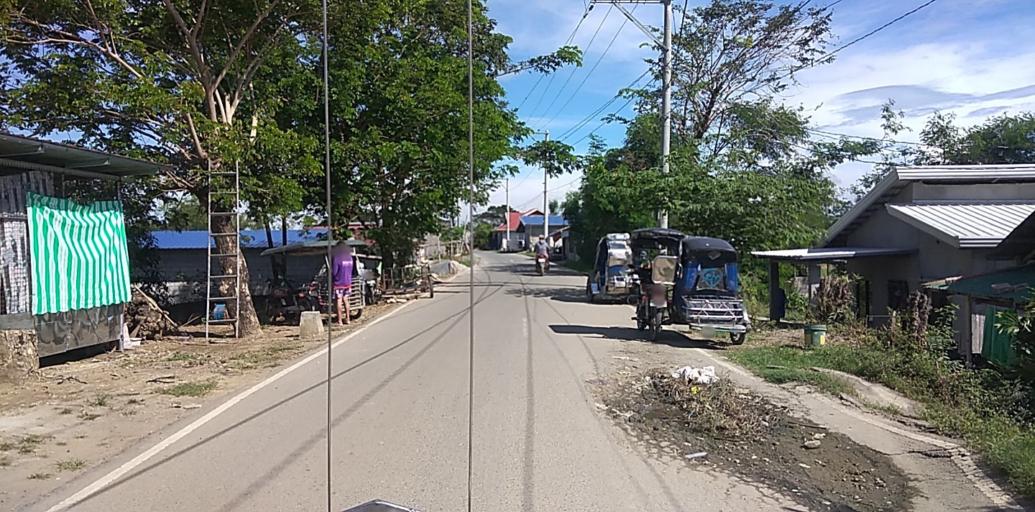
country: PH
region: Central Luzon
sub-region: Province of Pampanga
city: San Nicolas
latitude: 15.0672
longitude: 120.8050
